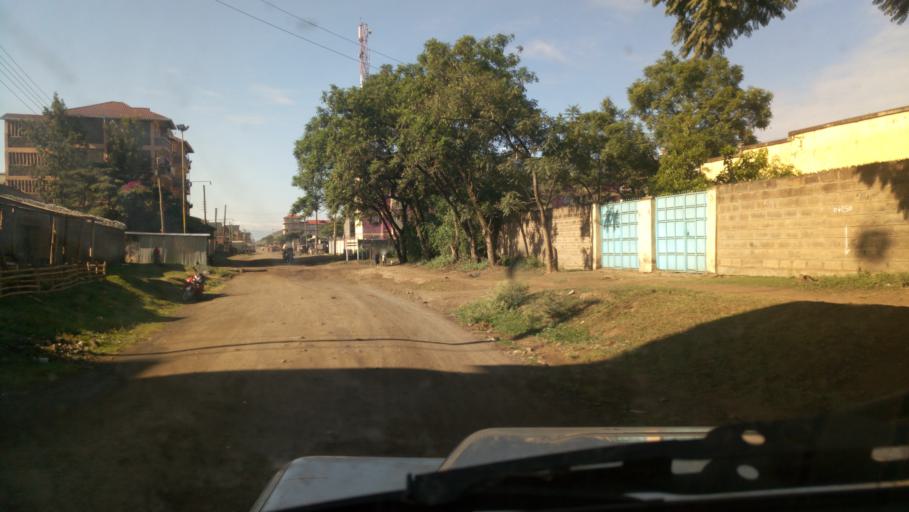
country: KE
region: Nakuru
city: Nakuru
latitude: -0.2981
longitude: 36.0703
